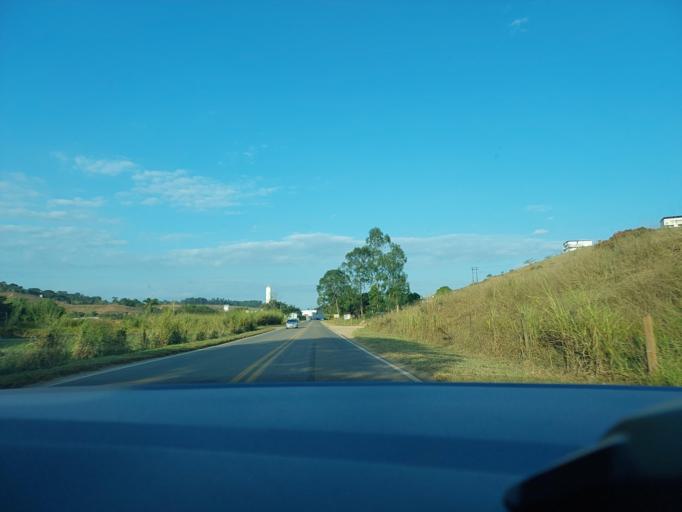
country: BR
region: Minas Gerais
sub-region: Muriae
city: Muriae
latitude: -21.1192
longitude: -42.4090
